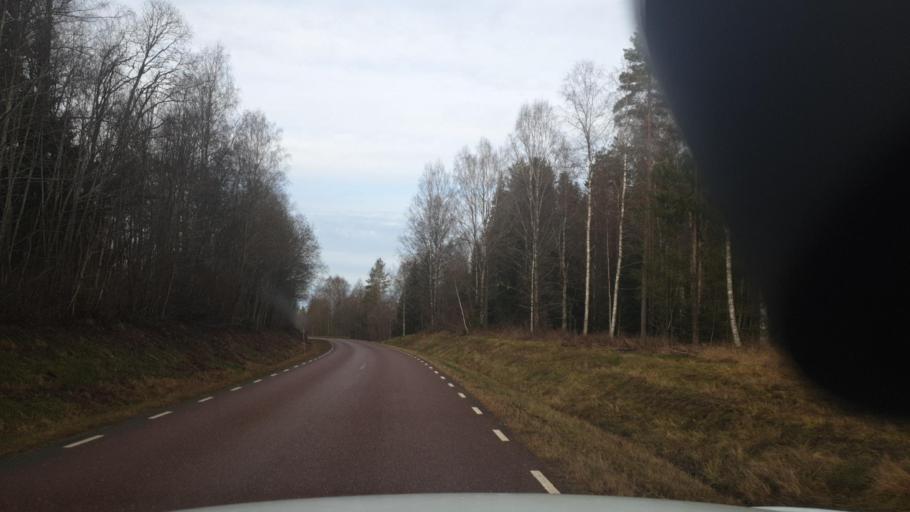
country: NO
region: Hedmark
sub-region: Eidskog
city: Skotterud
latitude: 59.7574
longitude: 12.0540
